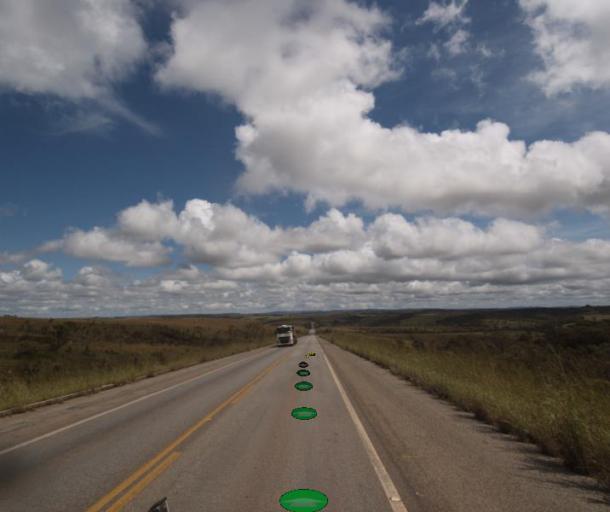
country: BR
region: Goias
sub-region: Abadiania
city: Abadiania
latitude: -15.7646
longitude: -48.4444
